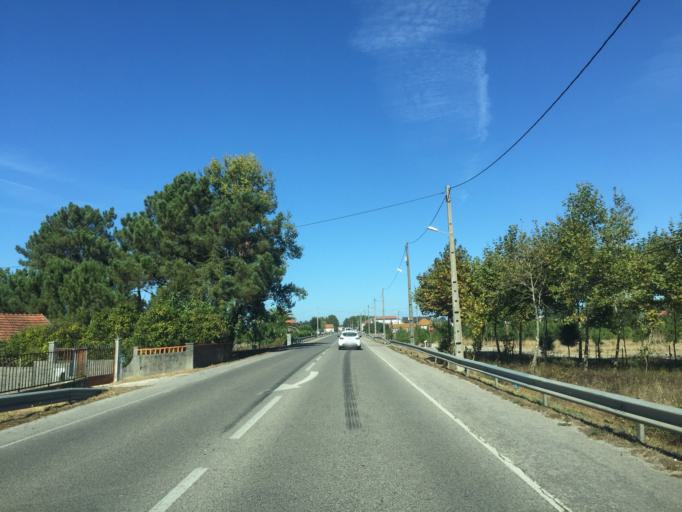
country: PT
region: Coimbra
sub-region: Figueira da Foz
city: Alhadas
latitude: 40.2595
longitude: -8.7796
